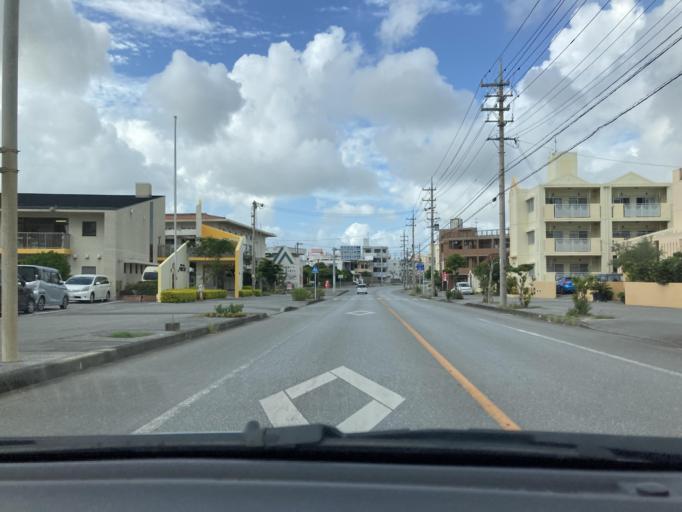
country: JP
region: Okinawa
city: Itoman
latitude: 26.1319
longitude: 127.6870
